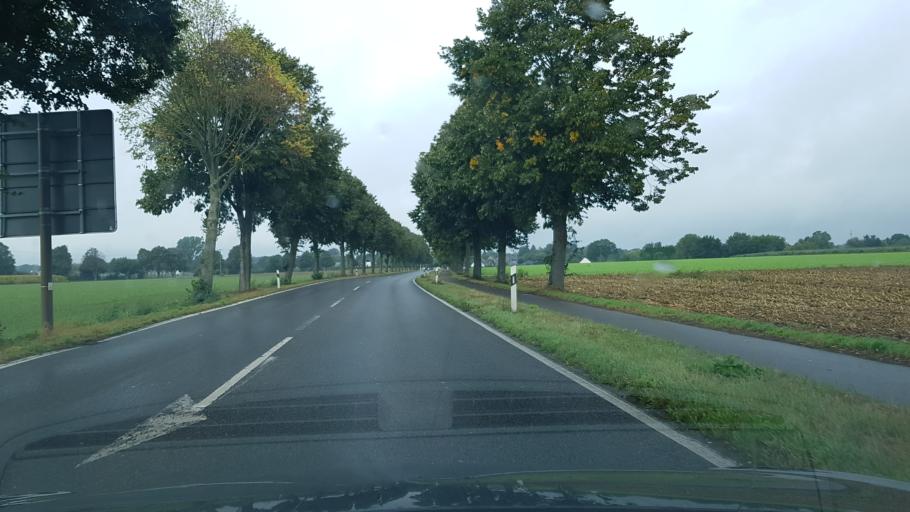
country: DE
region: North Rhine-Westphalia
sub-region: Regierungsbezirk Dusseldorf
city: Bruggen
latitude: 51.3080
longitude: 6.2096
